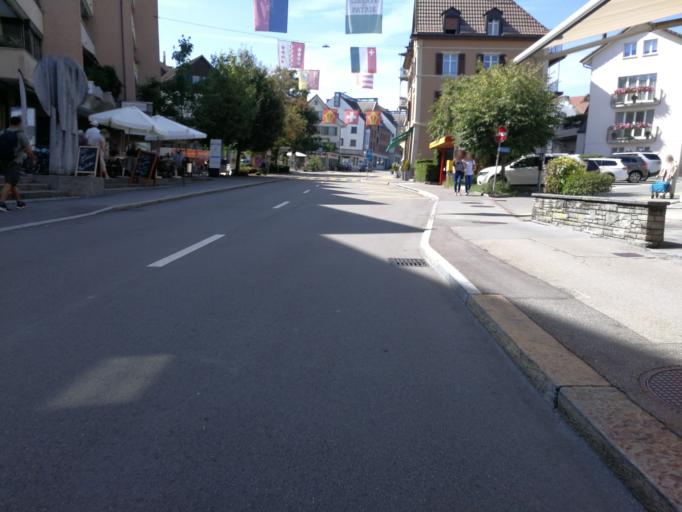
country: CH
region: Zurich
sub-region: Bezirk Horgen
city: Waedenswil / Dorf (Waedenswil)
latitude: 47.2298
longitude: 8.6707
